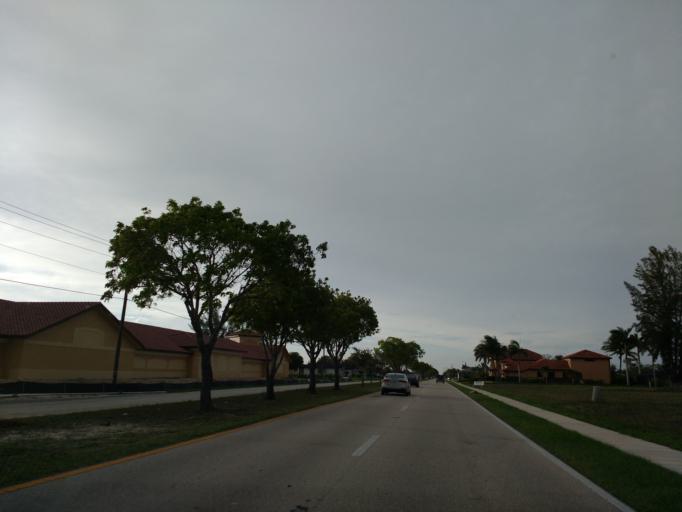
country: US
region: Florida
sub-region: Lee County
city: Cape Coral
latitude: 26.5678
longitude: -82.0067
